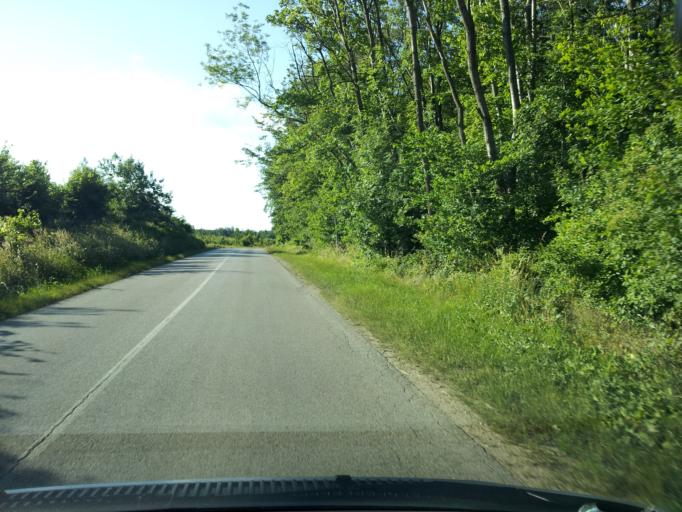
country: HU
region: Veszprem
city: Zirc
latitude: 47.2368
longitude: 17.8594
